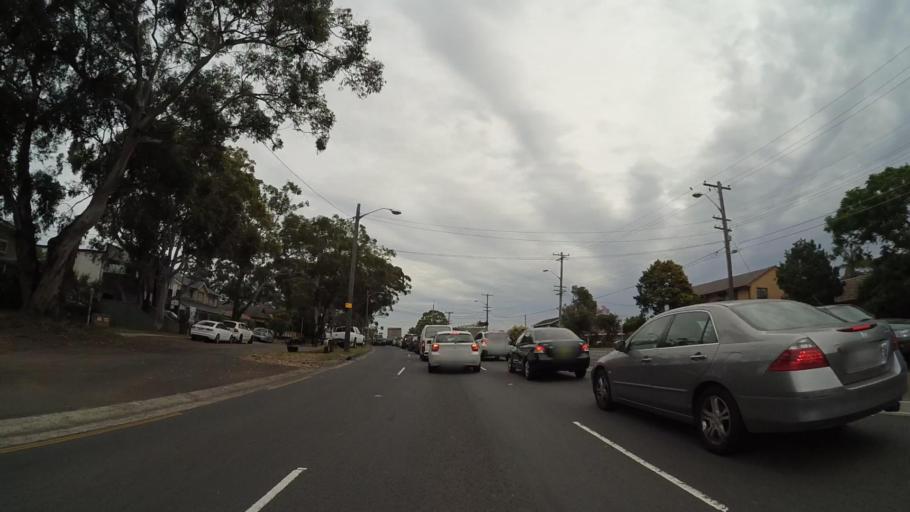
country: AU
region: New South Wales
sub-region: Sutherland Shire
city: Kareela
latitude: -34.0184
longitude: 151.0906
